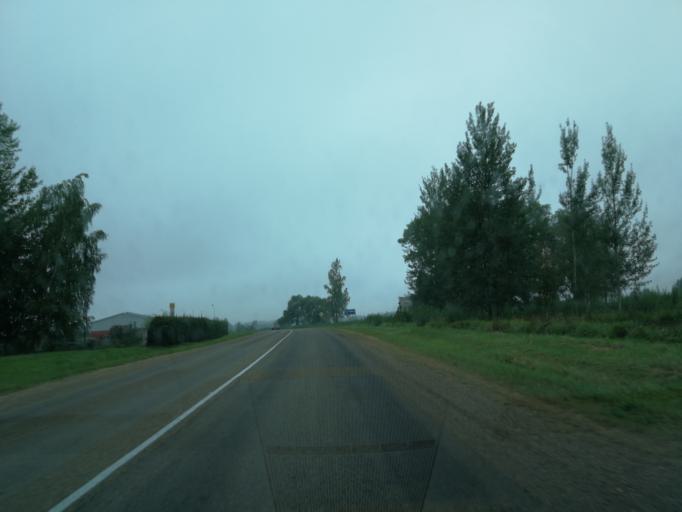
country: LV
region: Preilu Rajons
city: Preili
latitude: 56.2990
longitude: 26.7322
